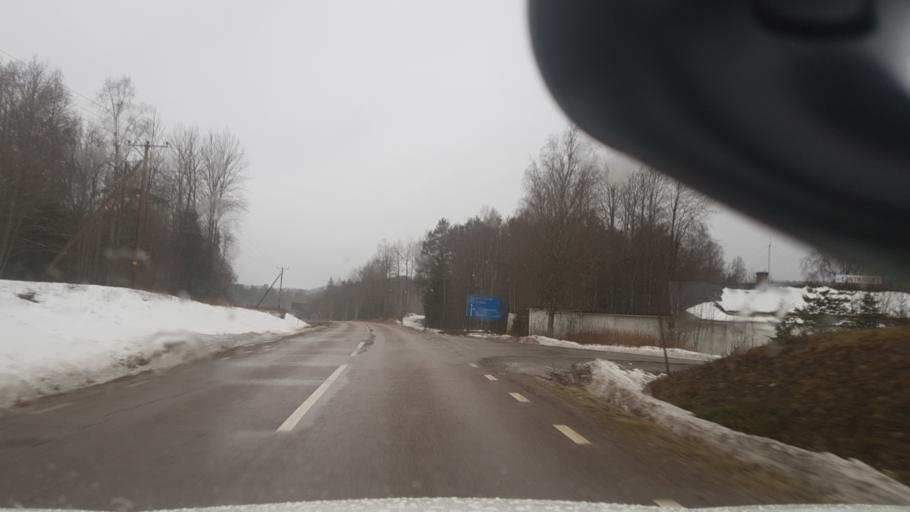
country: SE
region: Vaermland
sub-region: Arjangs Kommun
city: Arjaeng
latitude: 59.5566
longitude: 12.1272
